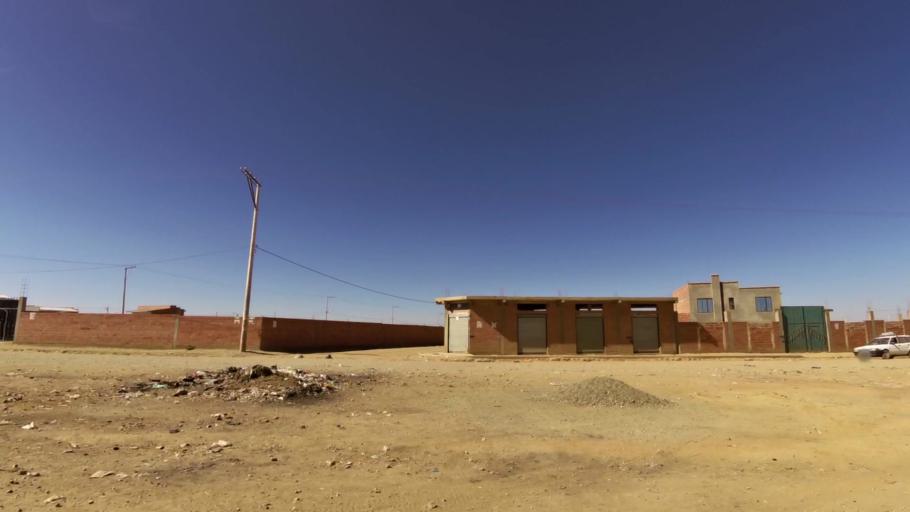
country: BO
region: La Paz
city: La Paz
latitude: -16.6255
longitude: -68.1942
